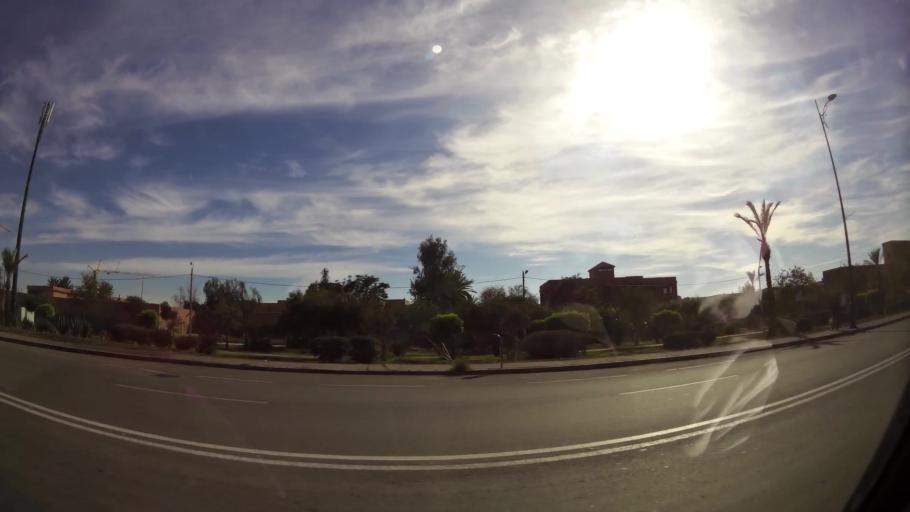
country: MA
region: Marrakech-Tensift-Al Haouz
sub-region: Marrakech
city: Marrakesh
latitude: 31.6683
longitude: -8.0378
